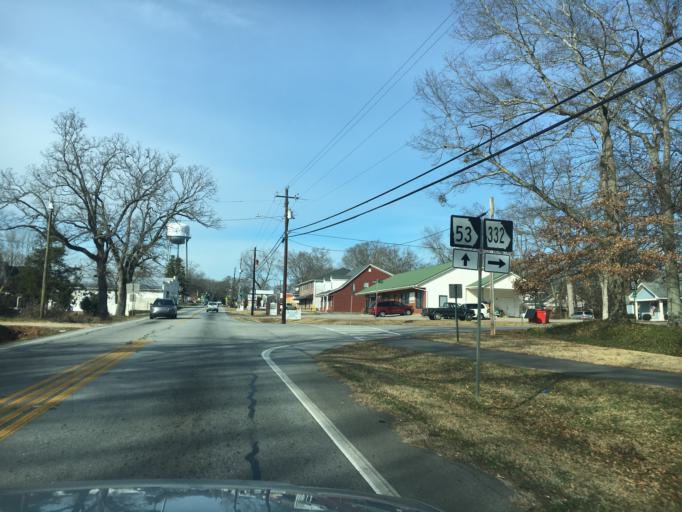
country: US
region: Georgia
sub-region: Jackson County
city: Hoschton
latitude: 34.0952
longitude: -83.7608
